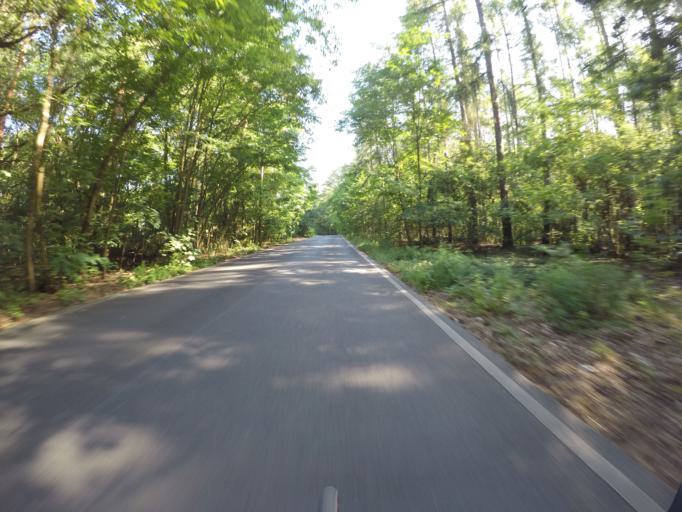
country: DE
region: Berlin
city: Schmockwitz
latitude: 52.3453
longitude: 13.6455
